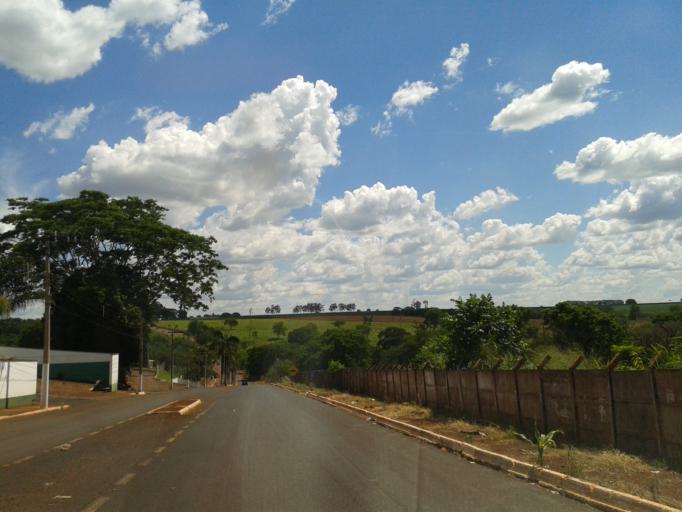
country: BR
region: Minas Gerais
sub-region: Centralina
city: Centralina
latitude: -18.7300
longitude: -49.2036
